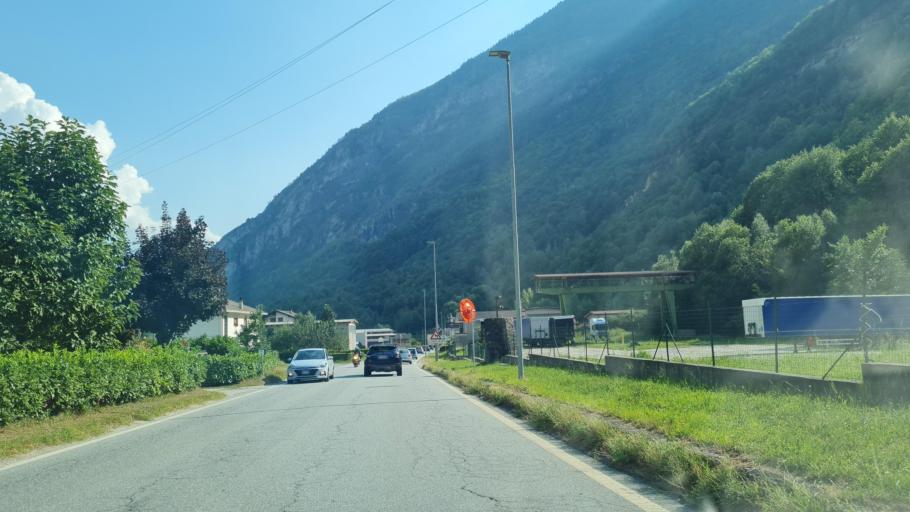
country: IT
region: Piedmont
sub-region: Provincia Verbano-Cusio-Ossola
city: Crodo
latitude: 46.2045
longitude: 8.3189
